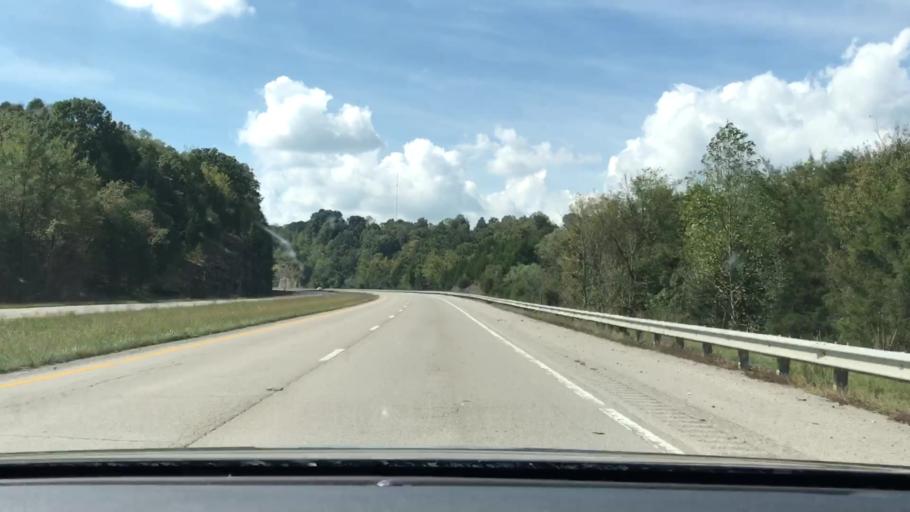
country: US
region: Kentucky
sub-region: Metcalfe County
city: Edmonton
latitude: 37.0269
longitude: -85.5464
